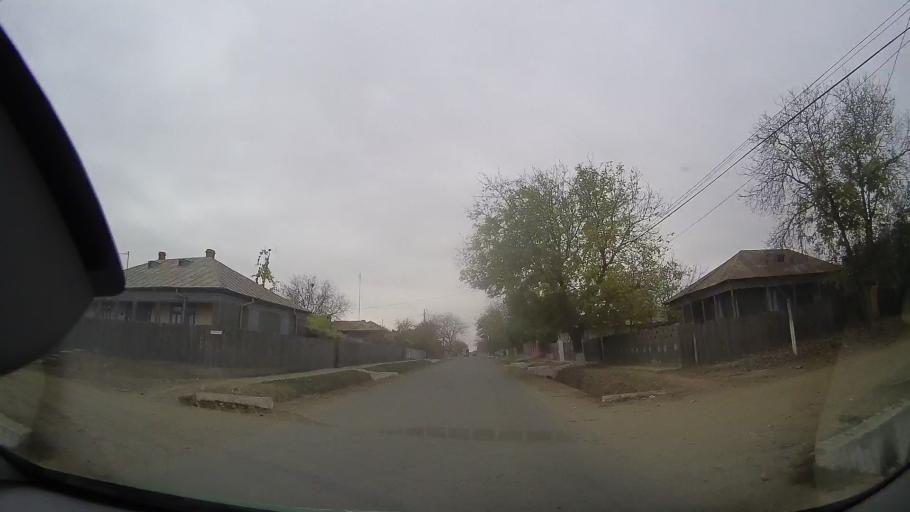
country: RO
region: Buzau
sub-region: Comuna Rusetu
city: Rusetu
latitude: 44.9637
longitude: 27.2115
